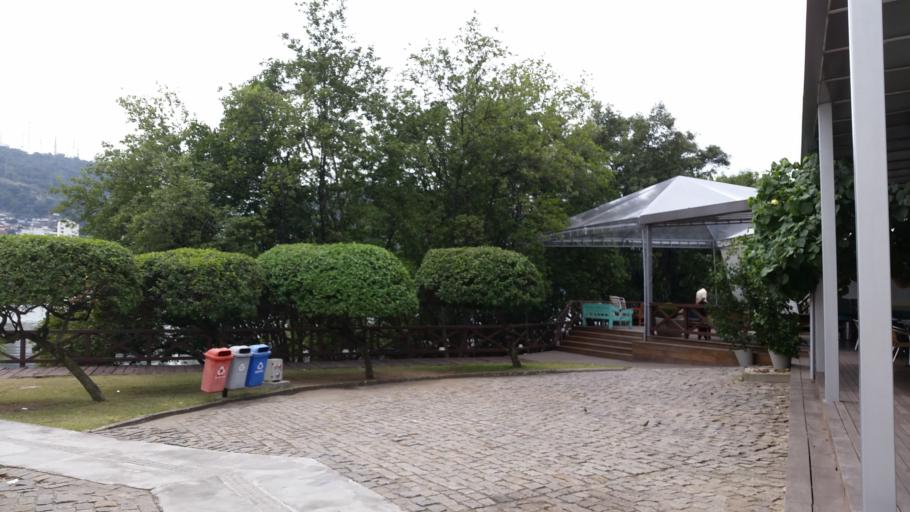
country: BR
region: Espirito Santo
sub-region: Vitoria
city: Vitoria
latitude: -20.3265
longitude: -40.3449
